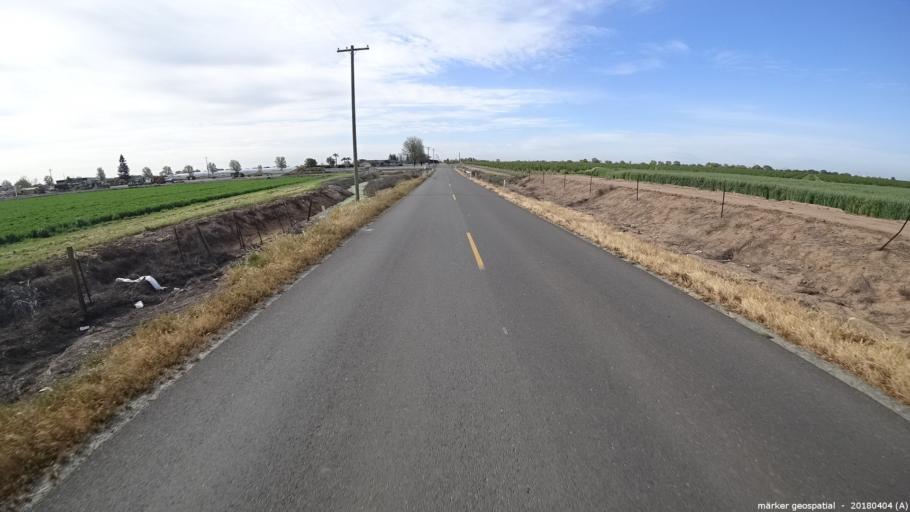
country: US
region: California
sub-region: Sacramento County
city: Herald
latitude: 38.3192
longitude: -121.3013
